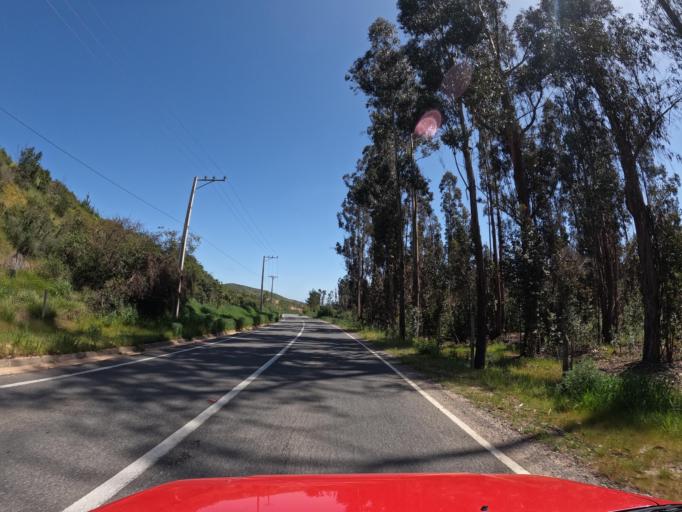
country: CL
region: O'Higgins
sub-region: Provincia de Colchagua
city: Santa Cruz
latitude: -34.6747
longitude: -71.8074
